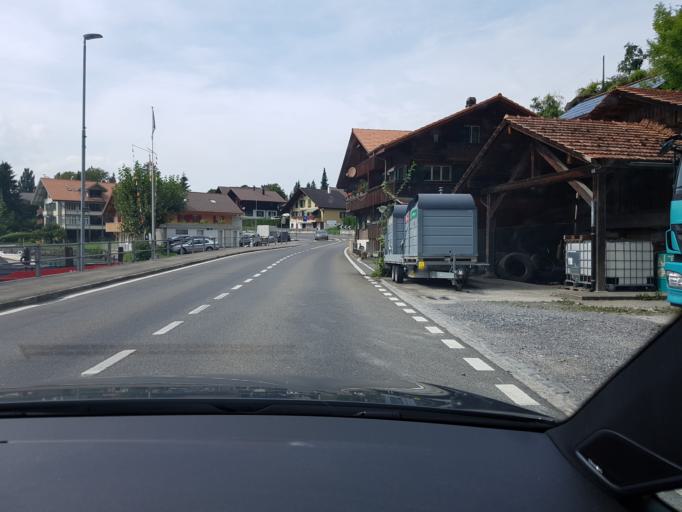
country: CH
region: Bern
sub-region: Thun District
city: Sigriswil
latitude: 46.6942
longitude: 7.7426
